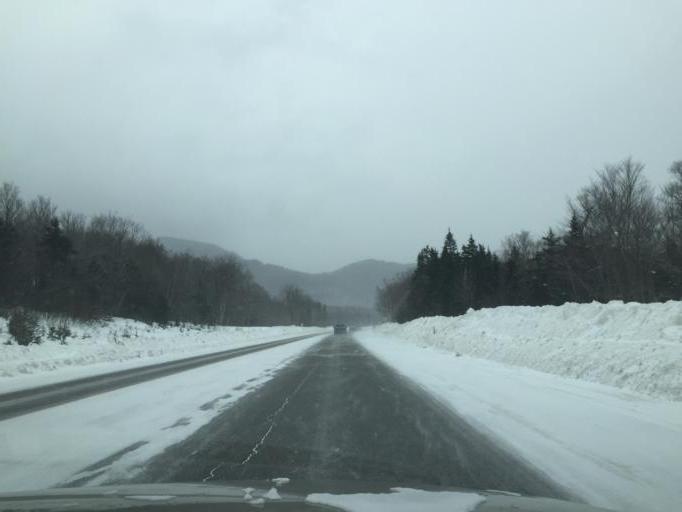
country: US
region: New Hampshire
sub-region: Coos County
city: Gorham
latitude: 44.2520
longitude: -71.2538
